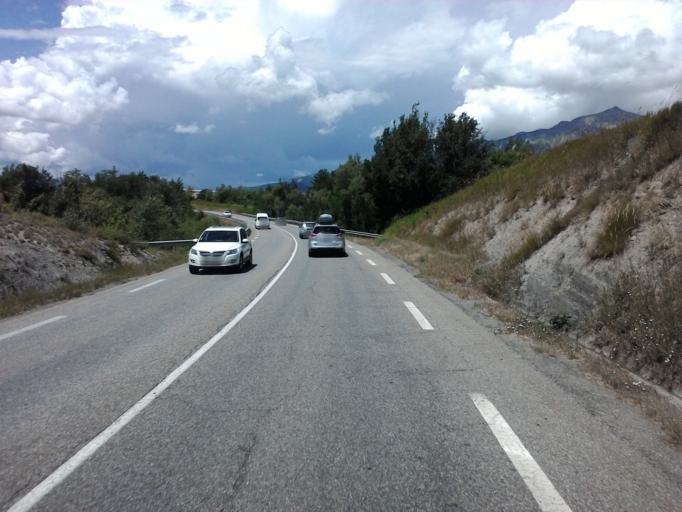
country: FR
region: Provence-Alpes-Cote d'Azur
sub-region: Departement des Hautes-Alpes
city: Chorges
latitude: 44.5371
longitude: 6.2982
